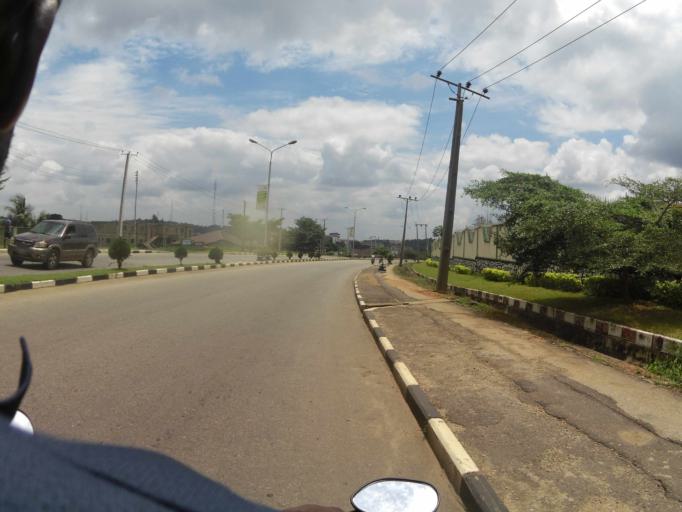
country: NG
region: Oyo
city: Ibadan
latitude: 7.4075
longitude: 3.9098
